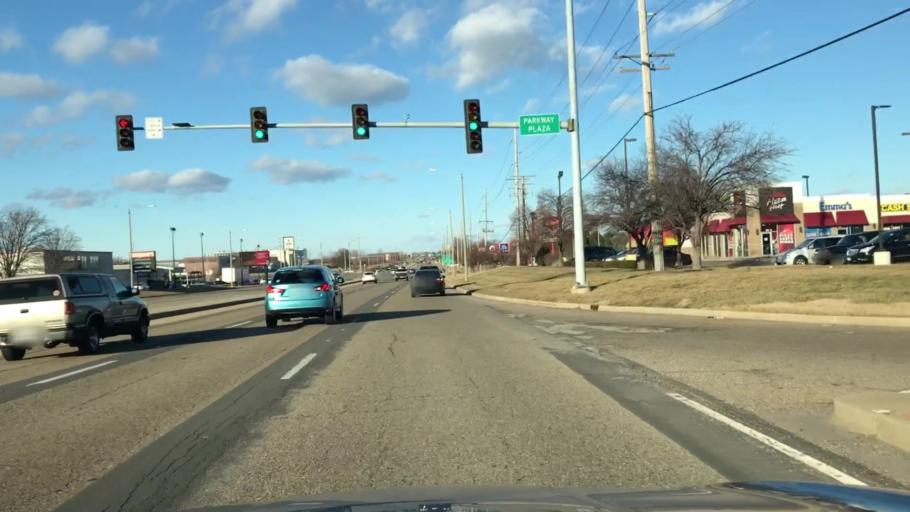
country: US
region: Illinois
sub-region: McLean County
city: Normal
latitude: 40.5142
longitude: -88.9531
